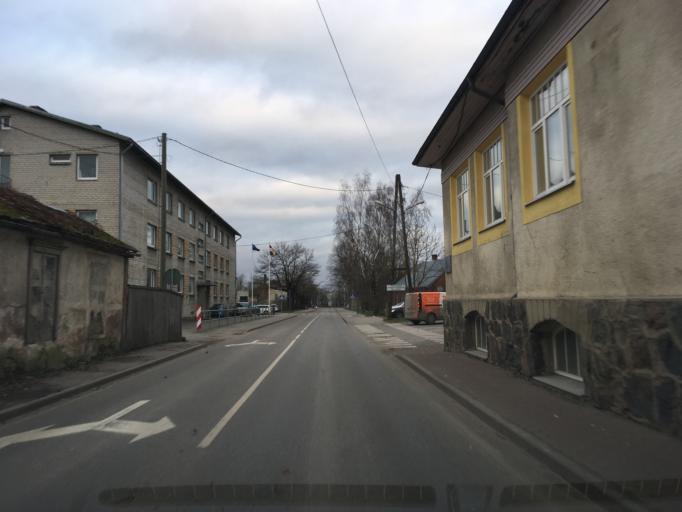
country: EE
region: Paernumaa
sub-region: Paernu linn
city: Parnu
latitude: 58.3868
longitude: 24.5107
